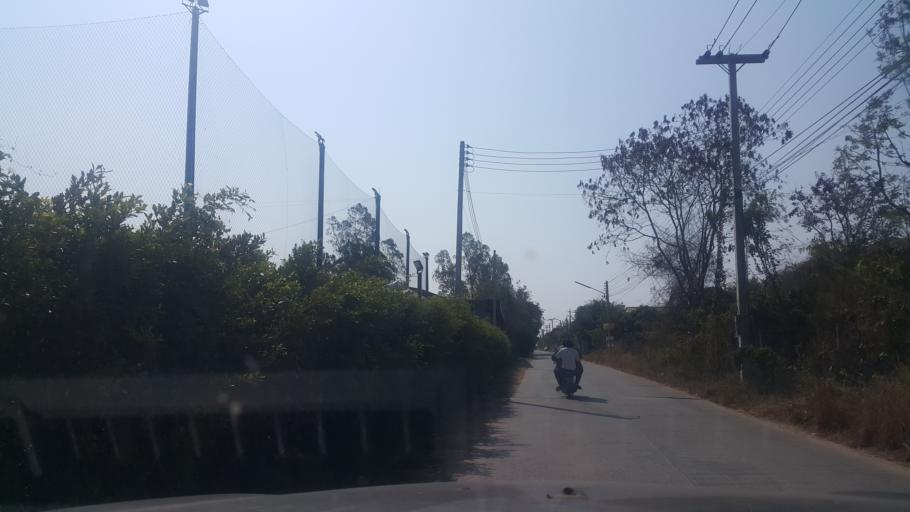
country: TH
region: Nakhon Ratchasima
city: Nakhon Ratchasima
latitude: 14.9352
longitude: 102.0367
